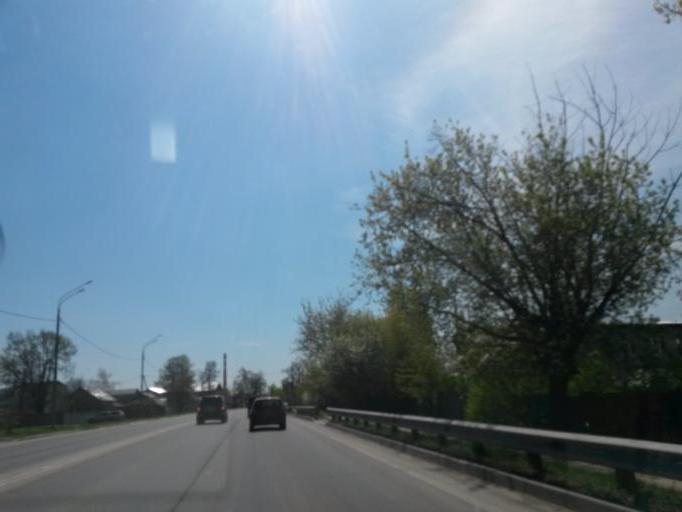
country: RU
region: Moskovskaya
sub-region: Podol'skiy Rayon
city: Podol'sk
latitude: 55.4026
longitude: 37.5514
